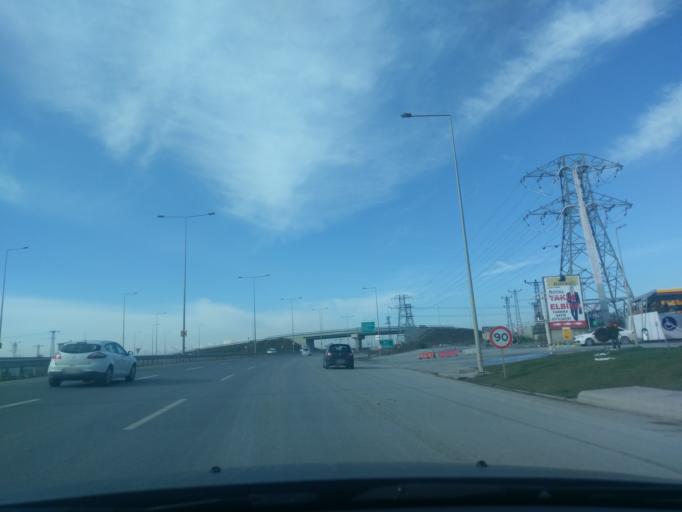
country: TR
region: Istanbul
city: Basaksehir
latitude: 41.1363
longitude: 28.8112
